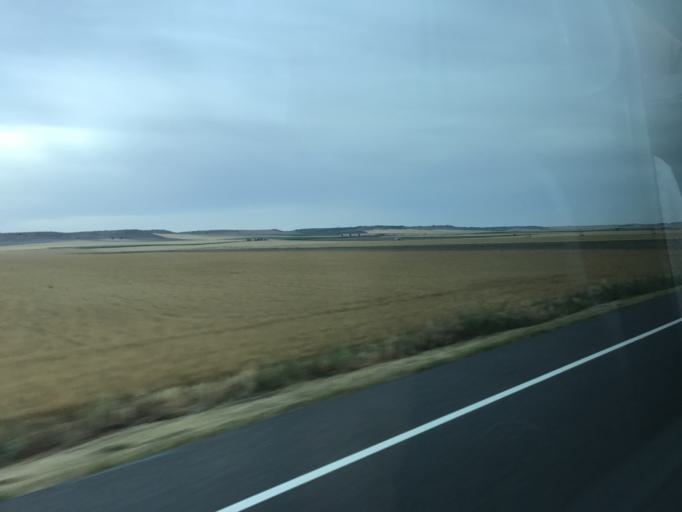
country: ES
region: Castille and Leon
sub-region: Provincia de Valladolid
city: Puras
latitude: 41.1680
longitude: -4.6558
